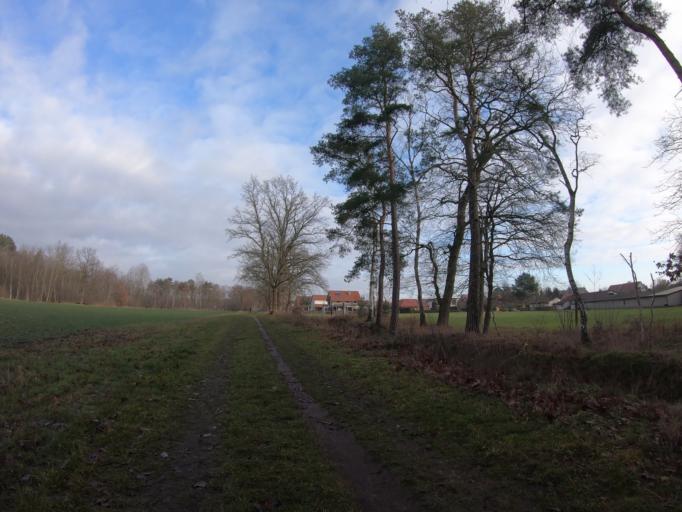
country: DE
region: Lower Saxony
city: Gifhorn
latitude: 52.4807
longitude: 10.5076
